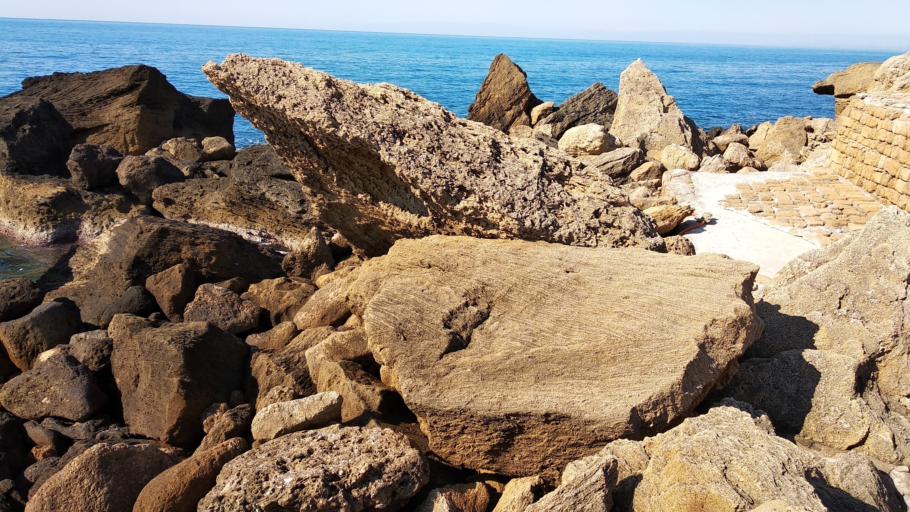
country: IT
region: Calabria
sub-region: Provincia di Crotone
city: Le Castella
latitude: 38.9059
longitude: 17.0222
